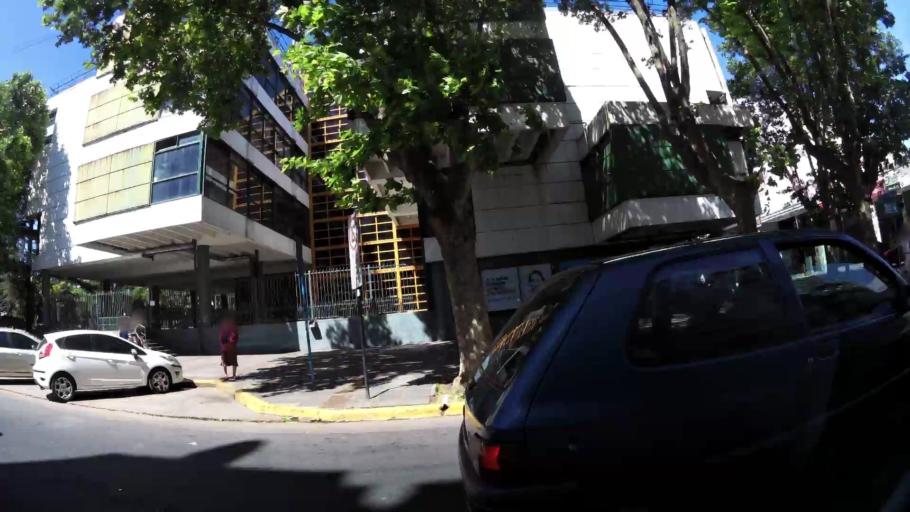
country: AR
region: Buenos Aires
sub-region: Partido de General San Martin
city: General San Martin
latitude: -34.5766
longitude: -58.5378
